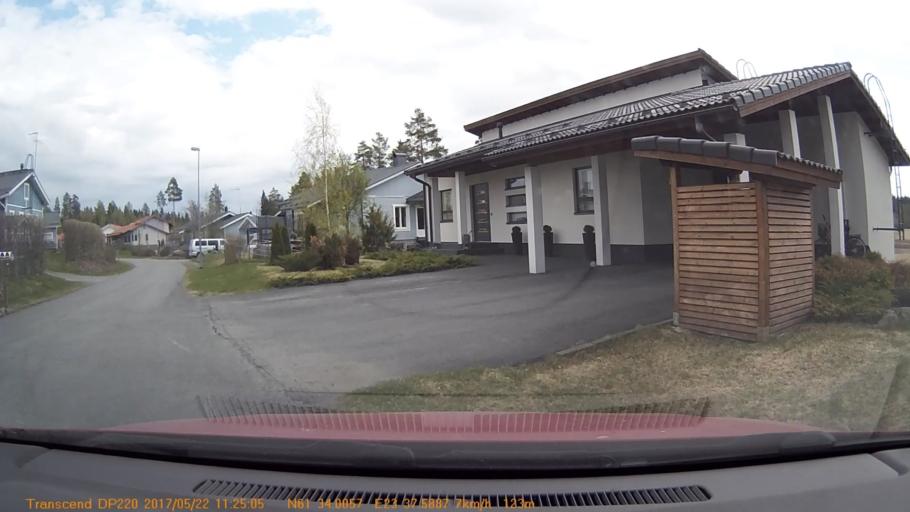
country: FI
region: Pirkanmaa
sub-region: Tampere
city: Yloejaervi
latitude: 61.5668
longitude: 23.6264
